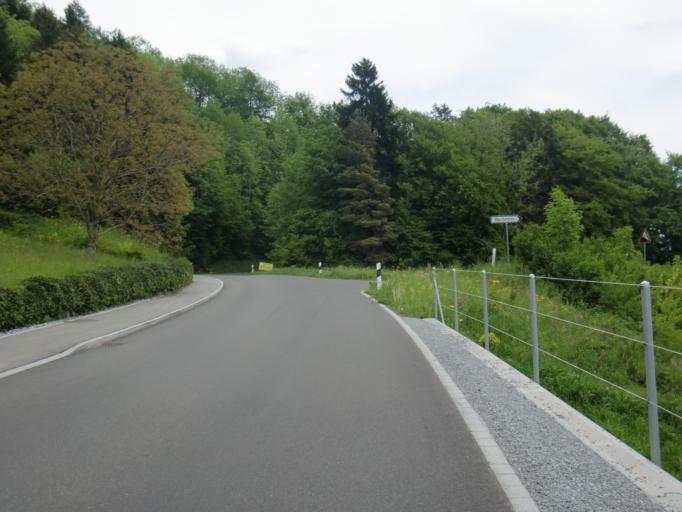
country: CH
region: Zurich
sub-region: Bezirk Hinwil
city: Hadlikon
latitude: 47.2843
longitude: 8.8754
